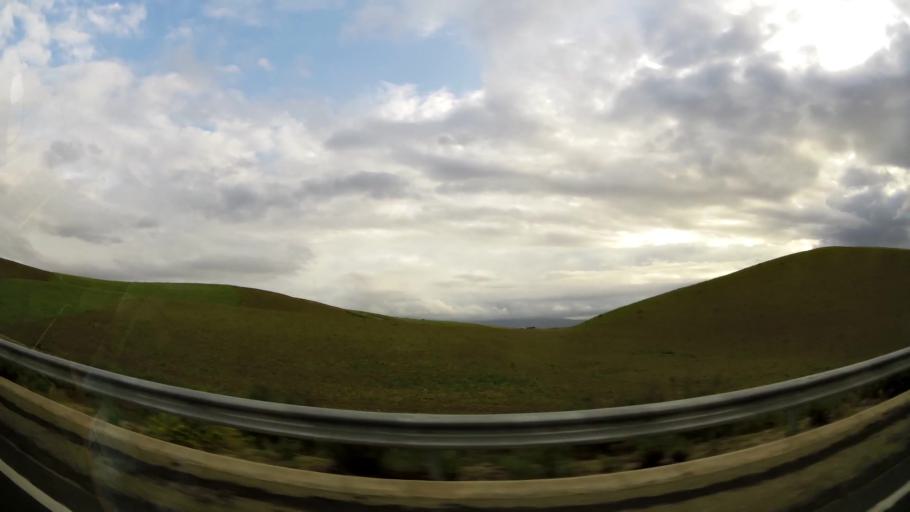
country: MA
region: Taza-Al Hoceima-Taounate
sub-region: Taza
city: Taza
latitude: 34.2551
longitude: -3.9300
